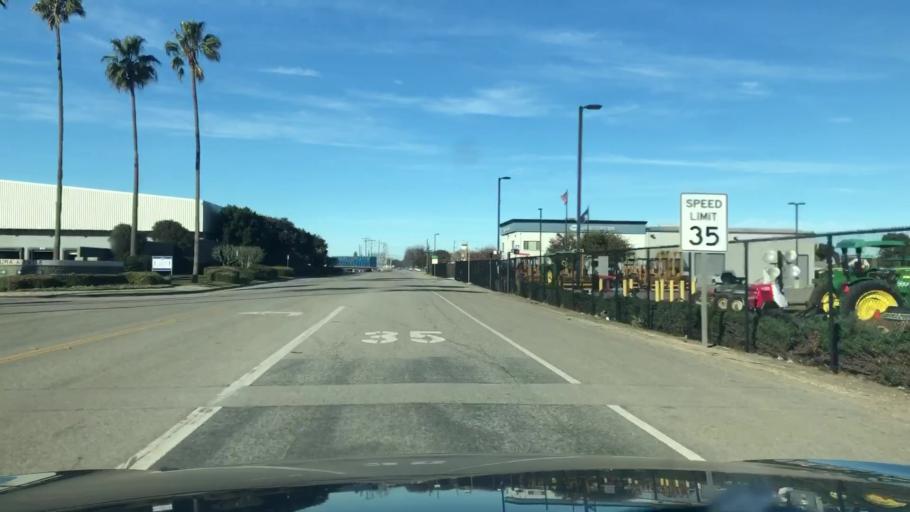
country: US
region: California
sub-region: Monterey County
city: Salinas
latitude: 36.6206
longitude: -121.6427
